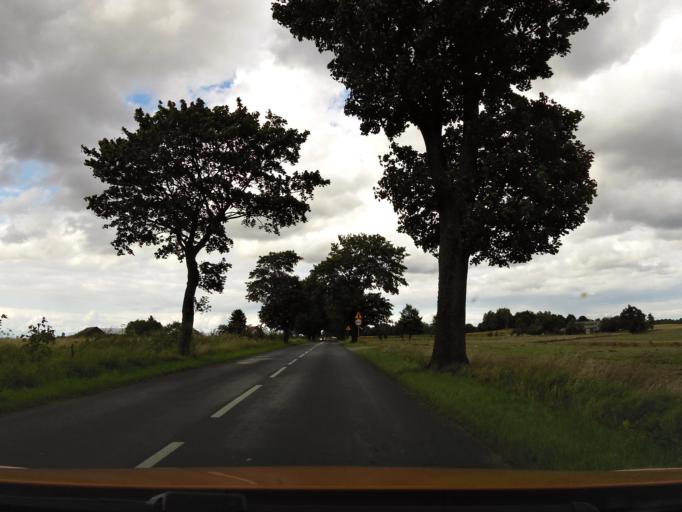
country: PL
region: West Pomeranian Voivodeship
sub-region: Powiat kolobrzeski
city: Ryman
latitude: 54.0434
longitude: 15.5447
